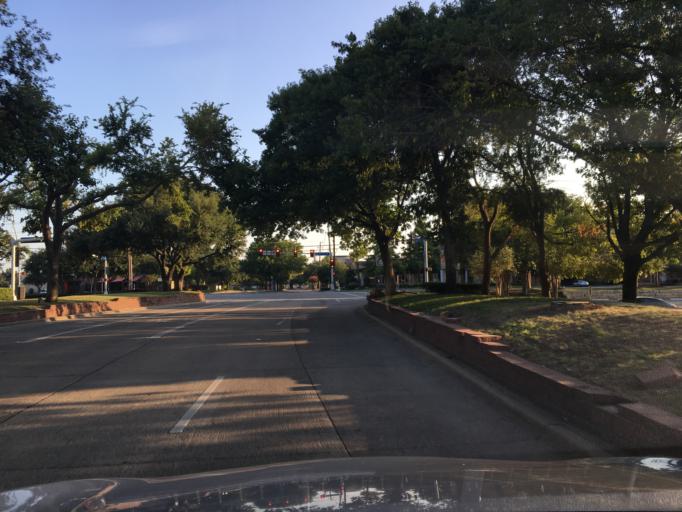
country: US
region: Texas
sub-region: Dallas County
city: Addison
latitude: 32.9530
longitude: -96.8259
